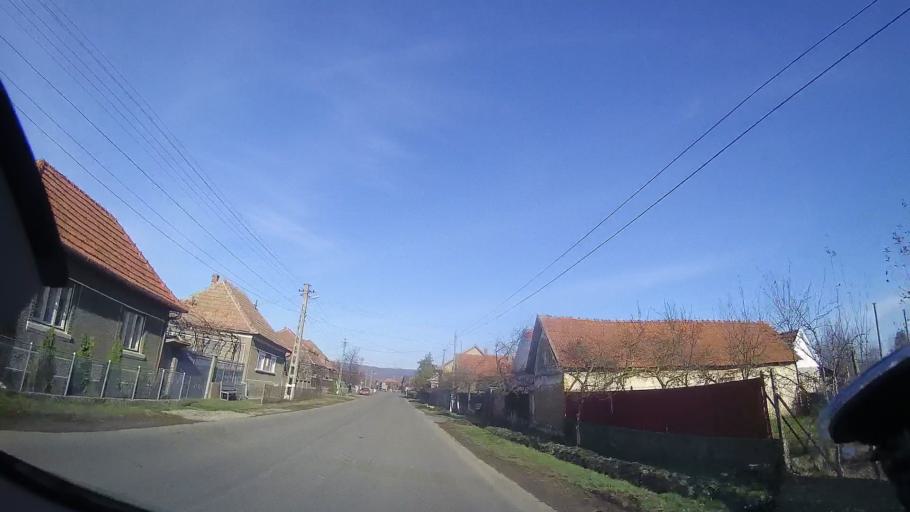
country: RO
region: Bihor
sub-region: Comuna Astileu
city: Astileu
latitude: 47.0305
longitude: 22.3879
